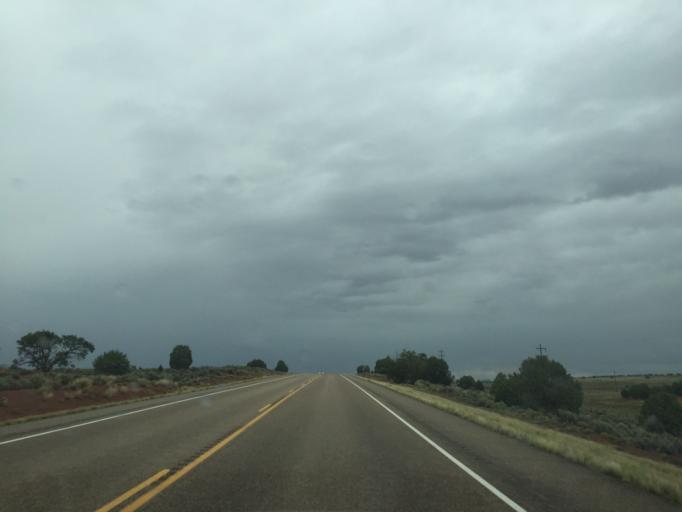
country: US
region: Utah
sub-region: Kane County
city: Kanab
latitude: 37.1433
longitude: -112.0721
